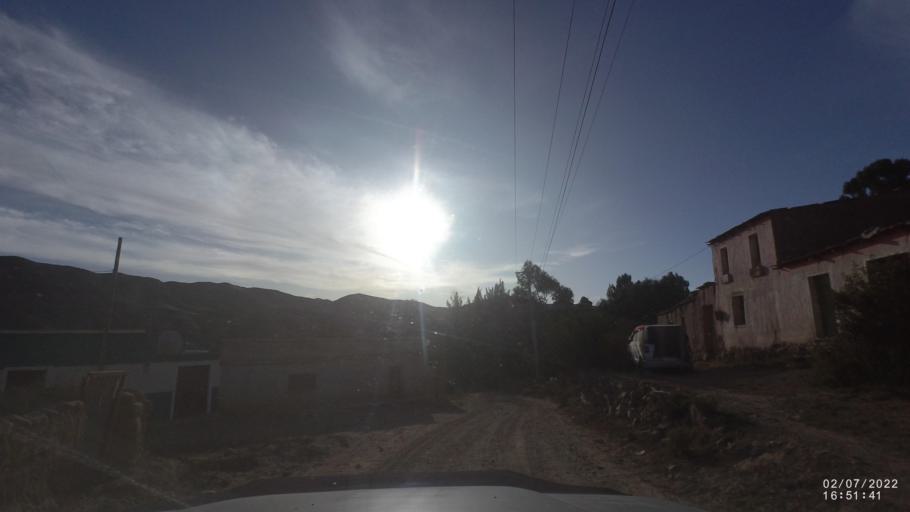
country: BO
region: Cochabamba
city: Irpa Irpa
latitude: -17.9693
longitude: -66.5351
